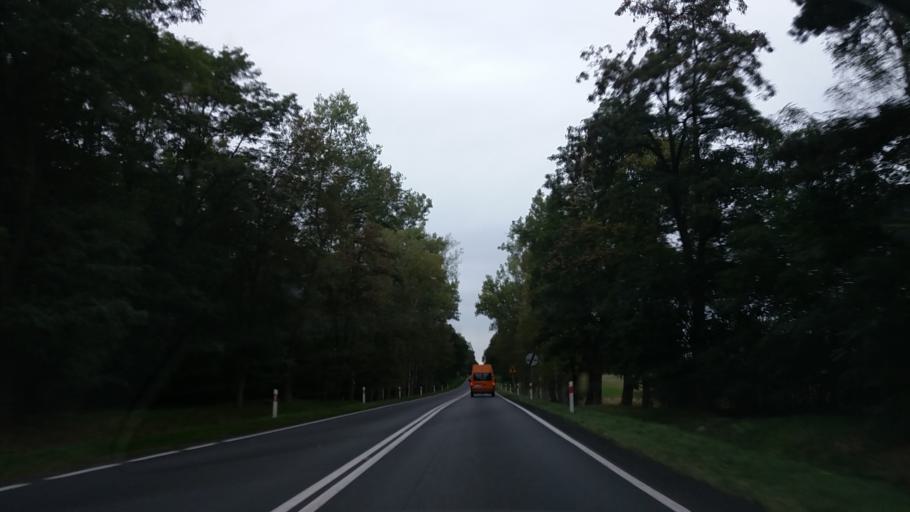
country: PL
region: Lower Silesian Voivodeship
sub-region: Powiat legnicki
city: Prochowice
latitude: 51.2997
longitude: 16.3375
